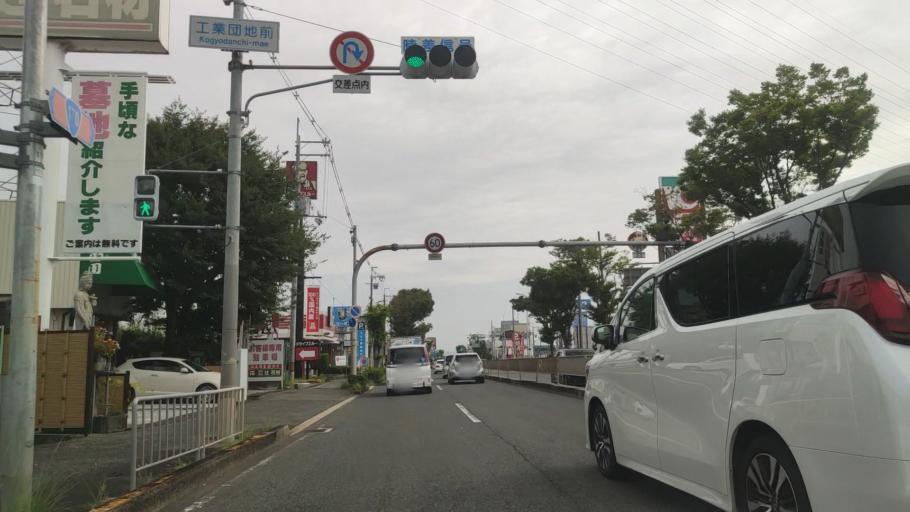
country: JP
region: Osaka
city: Tondabayashicho
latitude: 34.4482
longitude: 135.5564
